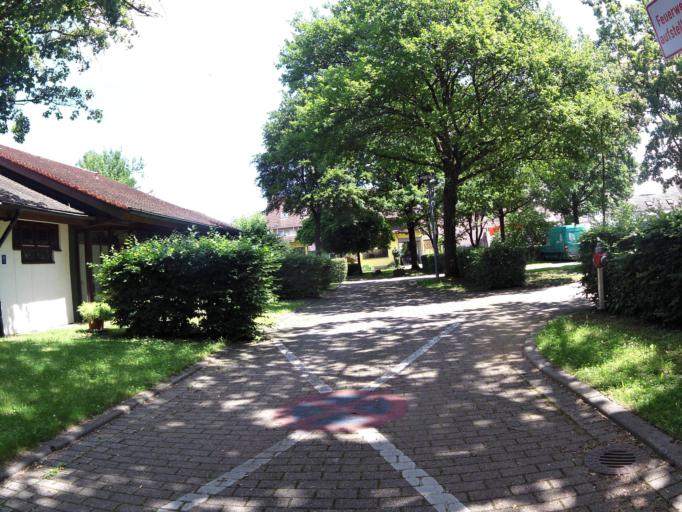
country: DE
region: Baden-Wuerttemberg
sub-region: Freiburg Region
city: Kippenheim
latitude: 48.3146
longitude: 7.8054
